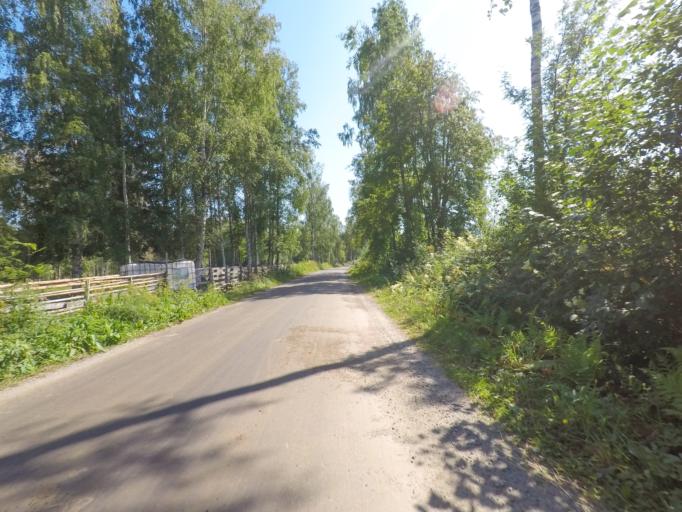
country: FI
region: Southern Savonia
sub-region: Mikkeli
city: Puumala
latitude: 61.4278
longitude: 28.0288
